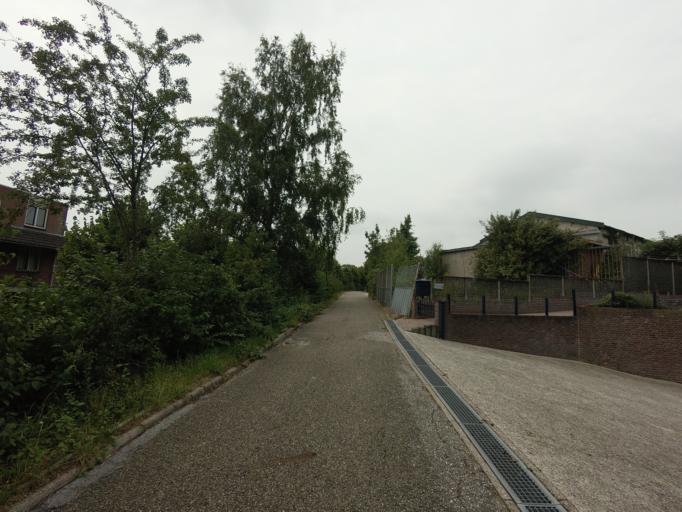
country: NL
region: Utrecht
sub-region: Gemeente Rhenen
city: Rhenen
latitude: 51.9565
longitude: 5.5717
